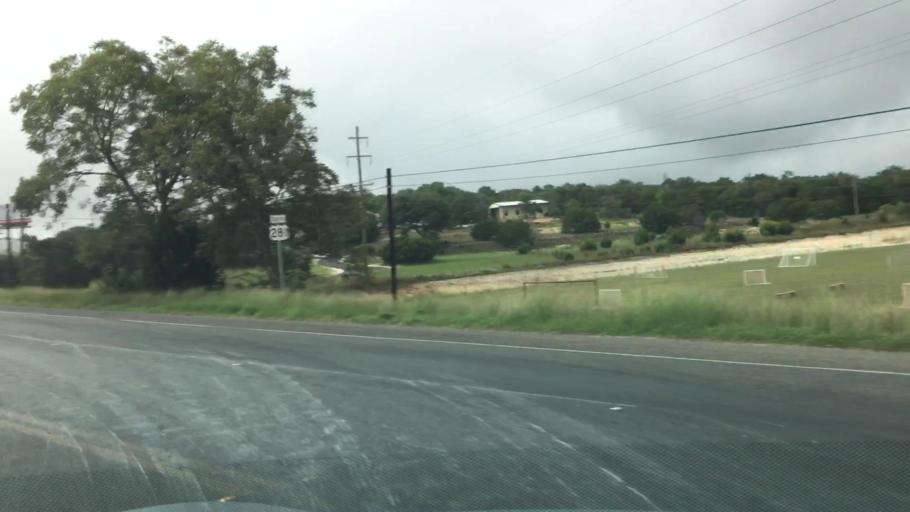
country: US
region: Texas
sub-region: Blanco County
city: Blanco
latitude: 30.0755
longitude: -98.4119
